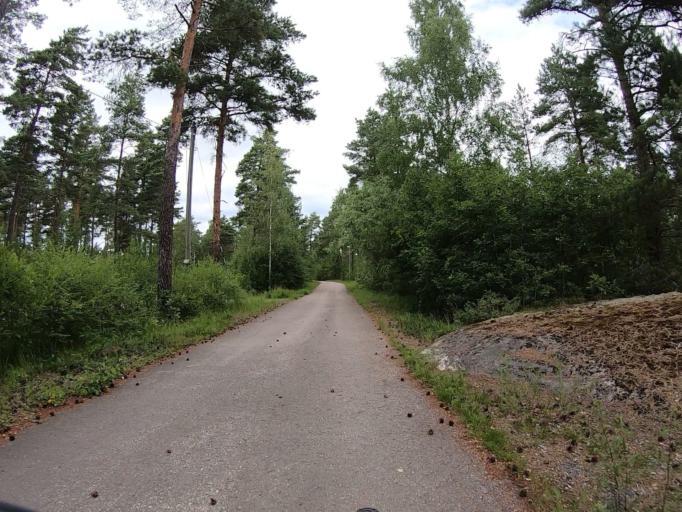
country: FI
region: Varsinais-Suomi
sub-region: Vakka-Suomi
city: Uusikaupunki
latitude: 60.8164
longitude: 21.4169
